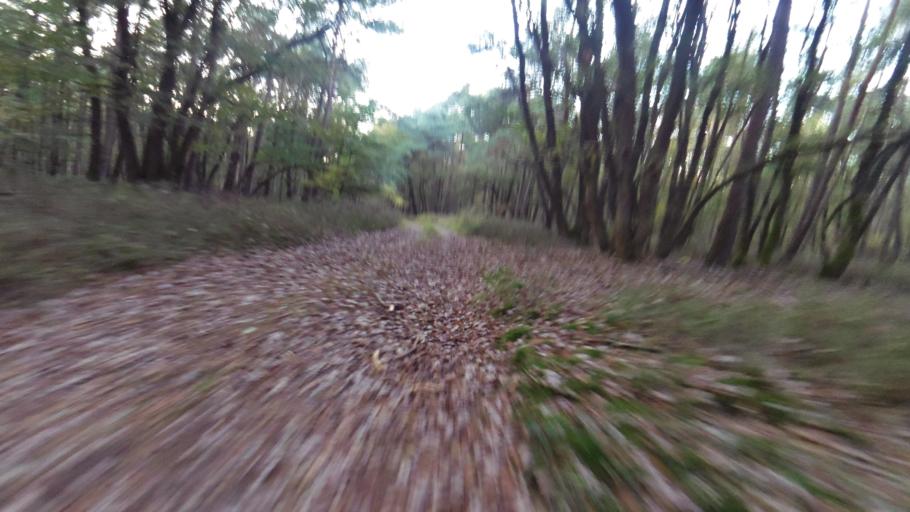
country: NL
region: Gelderland
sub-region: Gemeente Apeldoorn
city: Uddel
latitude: 52.2979
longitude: 5.8372
